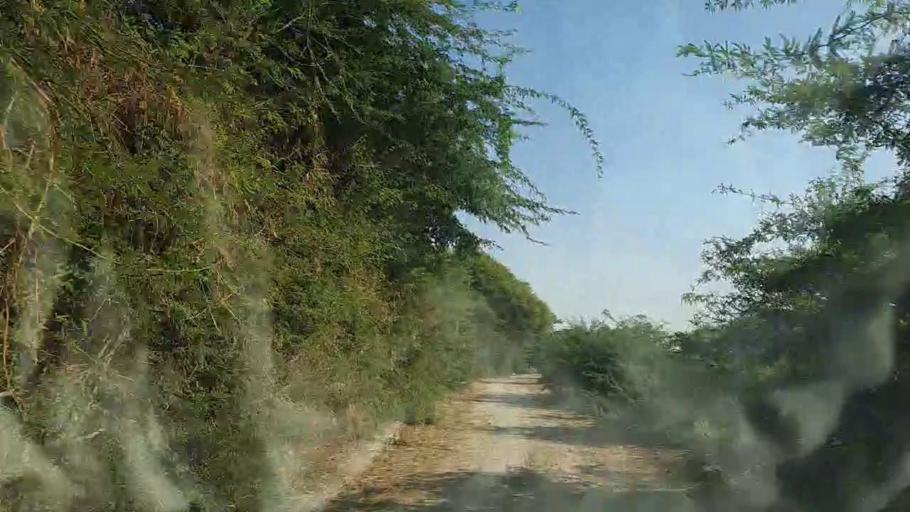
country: PK
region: Sindh
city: Mirpur Batoro
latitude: 24.6227
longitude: 68.1636
